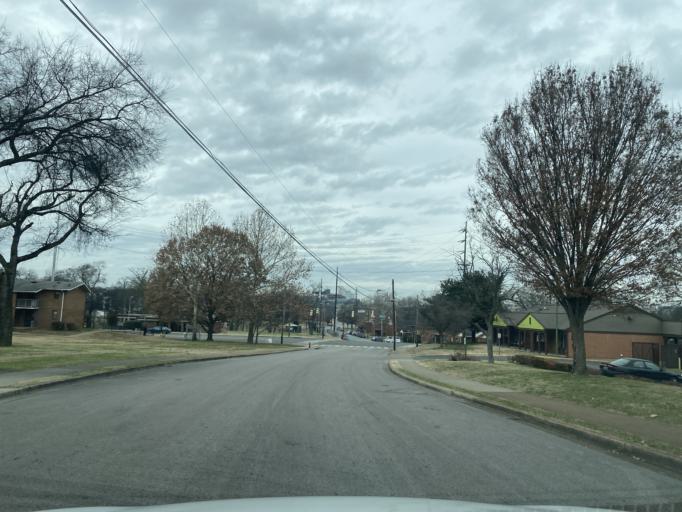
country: US
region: Tennessee
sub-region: Davidson County
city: Nashville
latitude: 36.1396
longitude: -86.7865
